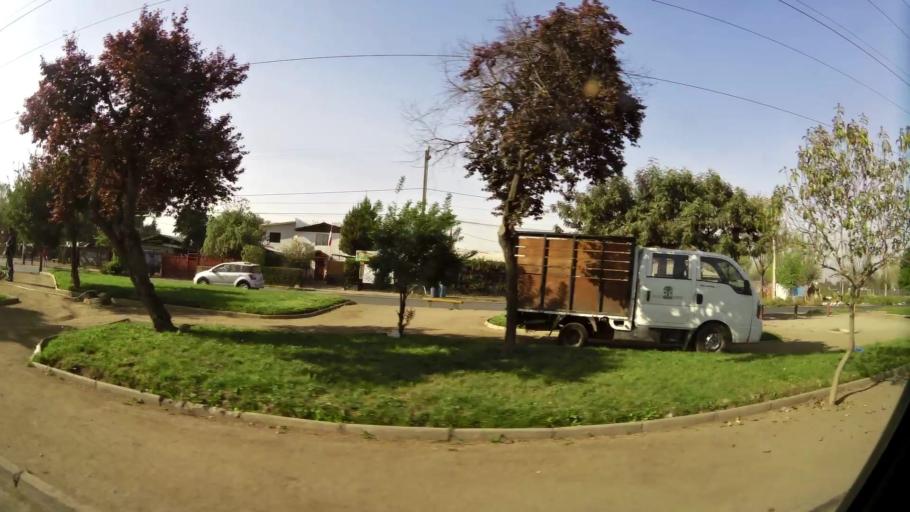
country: CL
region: Santiago Metropolitan
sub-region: Provincia de Santiago
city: Lo Prado
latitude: -33.4224
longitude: -70.7545
